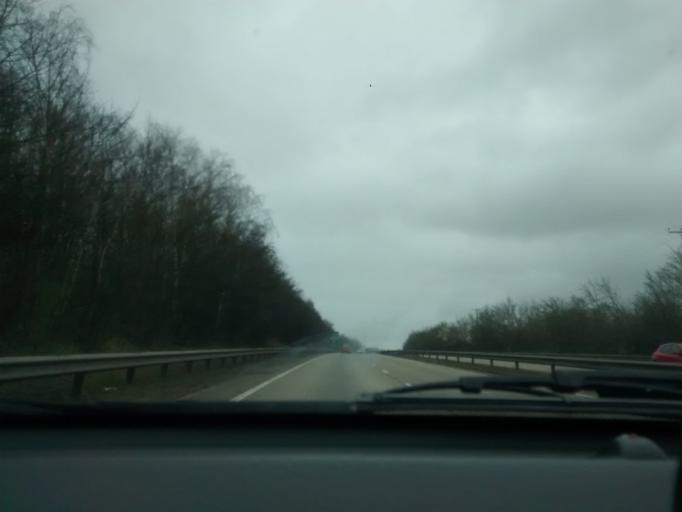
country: GB
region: England
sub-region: Suffolk
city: Bramford
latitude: 52.0728
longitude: 1.1112
